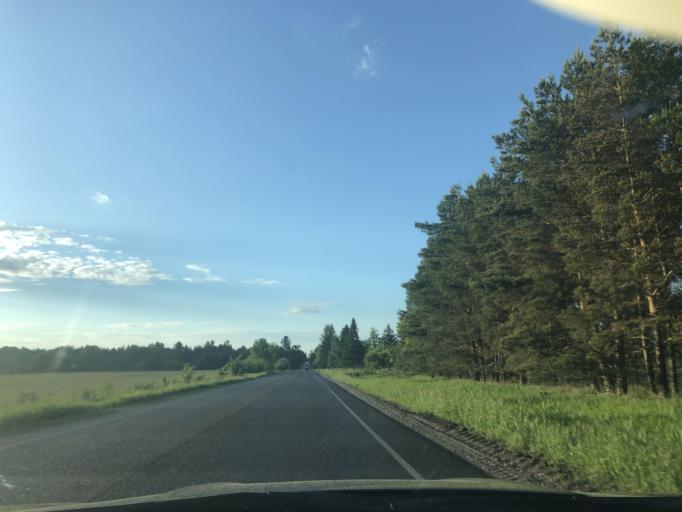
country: US
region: Michigan
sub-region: Missaukee County
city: Lake City
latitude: 44.3421
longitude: -85.0754
